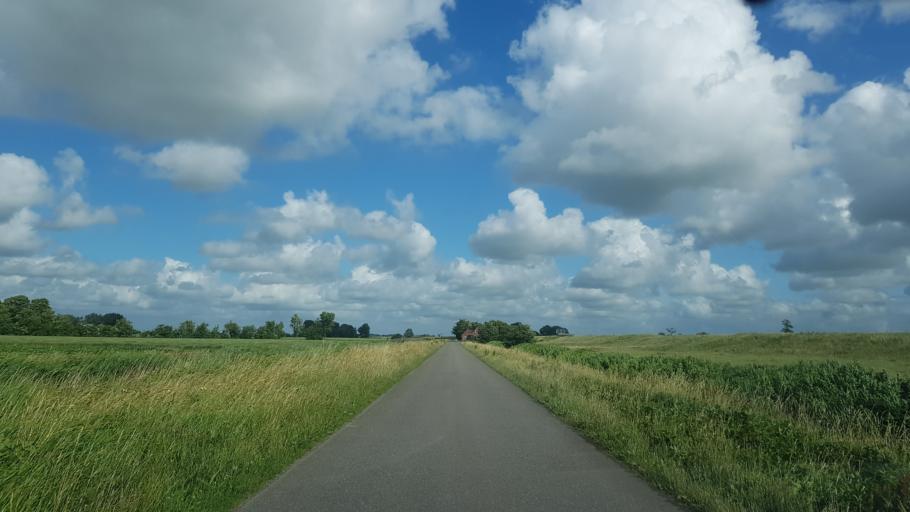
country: NL
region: Groningen
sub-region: Gemeente Winsum
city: Winsum
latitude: 53.4085
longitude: 6.5117
